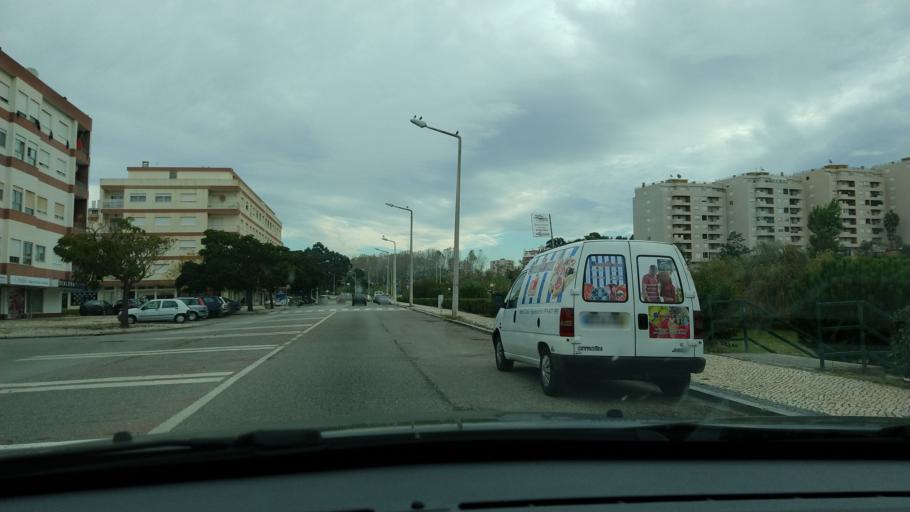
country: PT
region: Coimbra
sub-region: Figueira da Foz
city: Figueira da Foz
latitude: 40.1586
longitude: -8.8595
